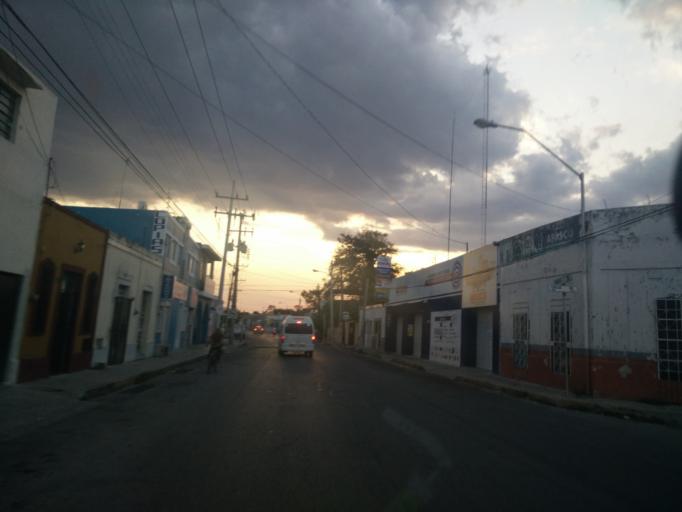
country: MX
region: Yucatan
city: Merida
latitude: 20.9638
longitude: -89.6371
